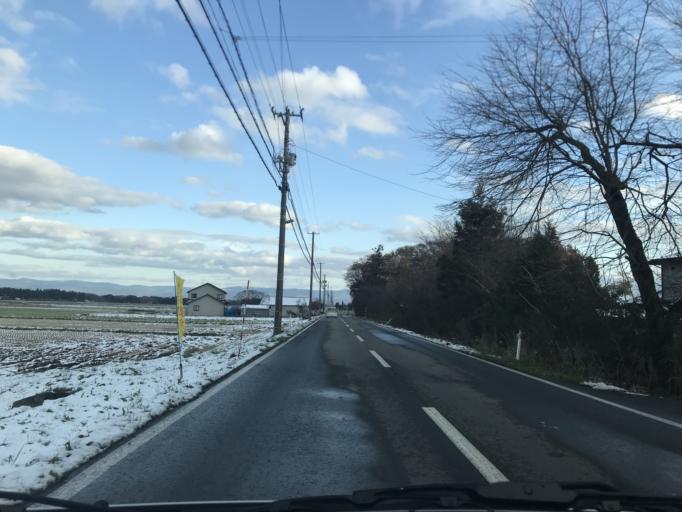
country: JP
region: Iwate
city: Kitakami
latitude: 39.2112
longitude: 141.0326
